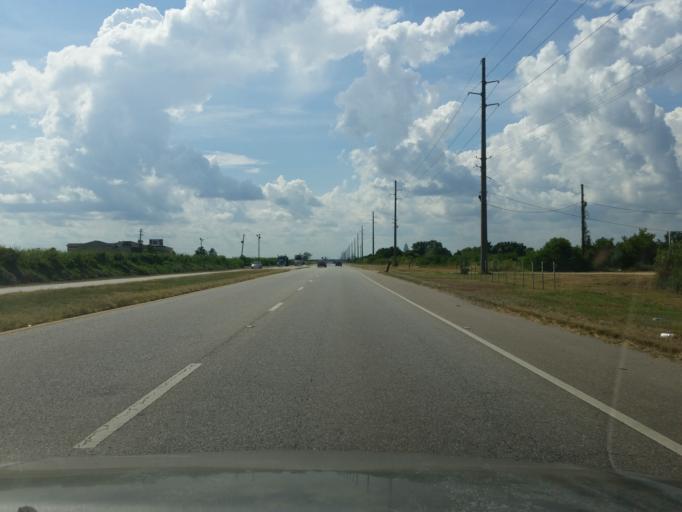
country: US
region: Alabama
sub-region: Baldwin County
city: Spanish Fort
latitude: 30.6742
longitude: -87.9625
